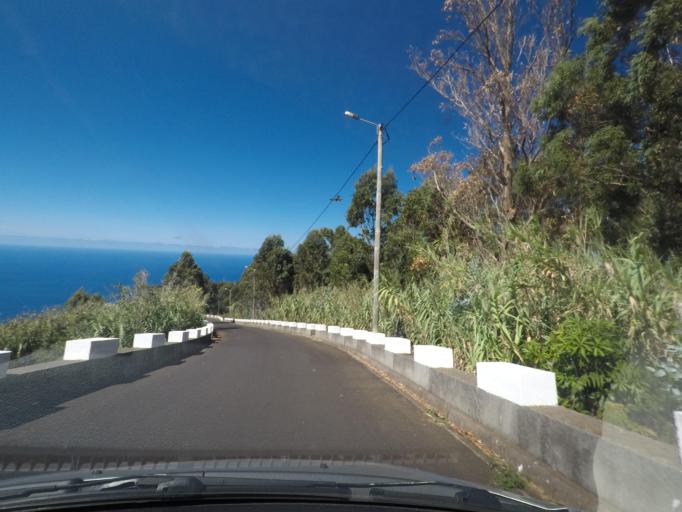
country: PT
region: Madeira
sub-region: Porto Moniz
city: Porto Moniz
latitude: 32.8582
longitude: -17.2011
